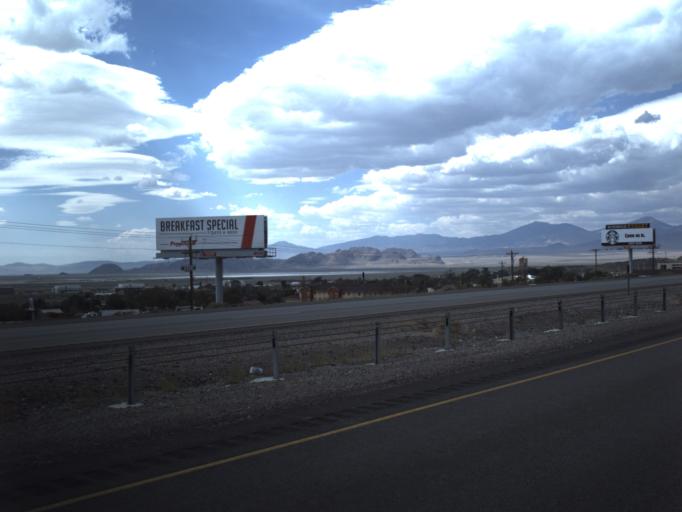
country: US
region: Utah
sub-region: Tooele County
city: Wendover
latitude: 40.7415
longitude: -114.0318
